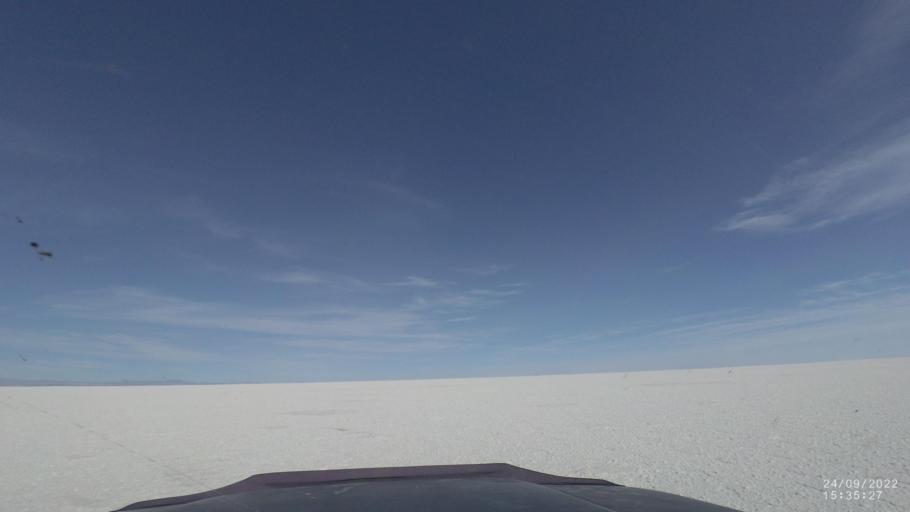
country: BO
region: Potosi
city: Colchani
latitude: -20.1354
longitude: -67.2541
